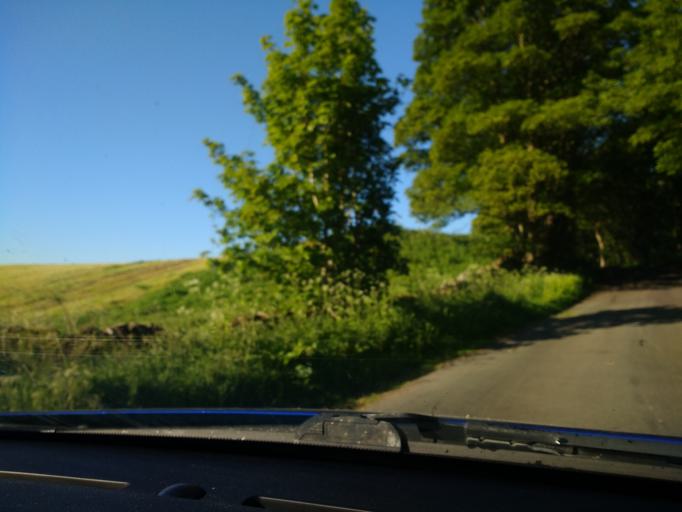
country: GB
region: England
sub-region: Cumbria
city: Appleby-in-Westmorland
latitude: 54.6687
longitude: -2.5960
